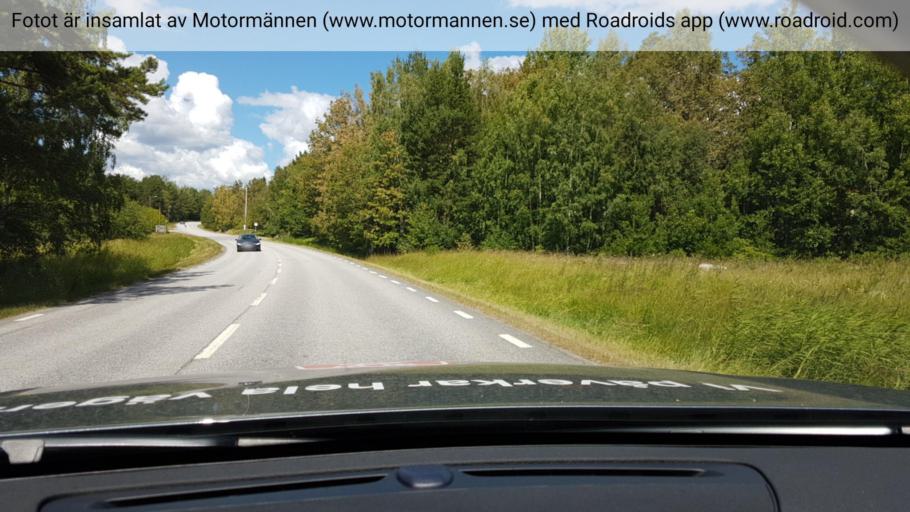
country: SE
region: Stockholm
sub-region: Varmdo Kommun
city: Hemmesta
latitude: 59.3389
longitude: 18.4864
